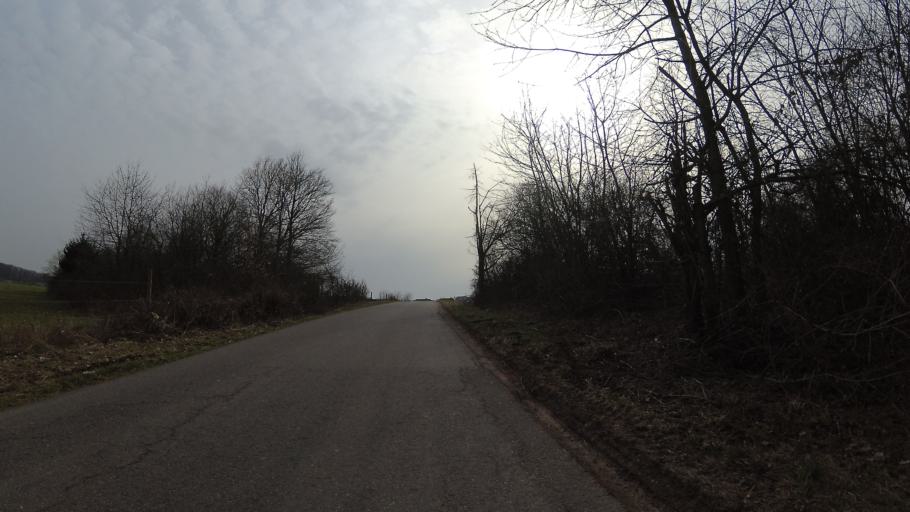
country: DE
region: Saarland
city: Nalbach
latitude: 49.4236
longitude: 6.7661
